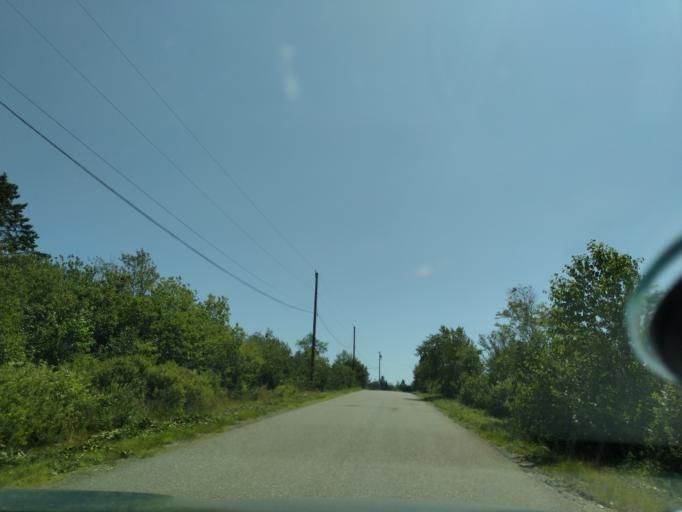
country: US
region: Maine
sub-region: Washington County
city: Eastport
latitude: 44.8302
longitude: -67.0054
